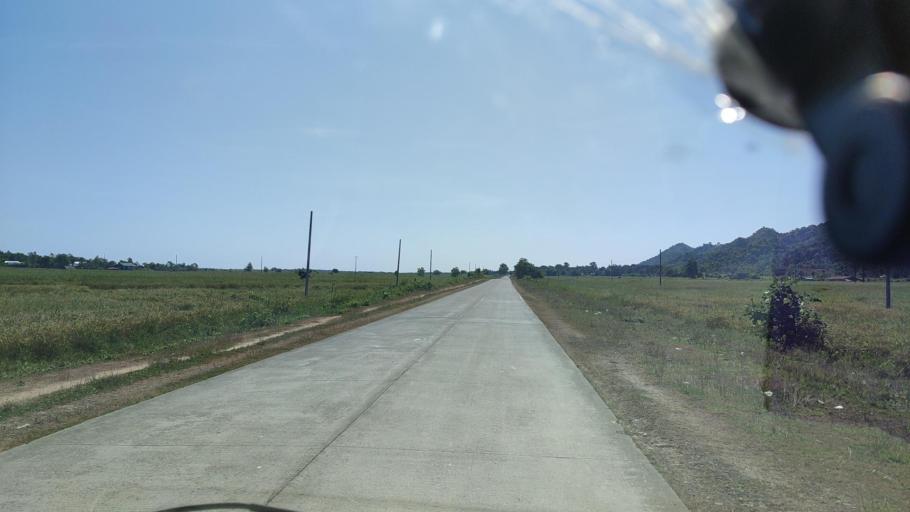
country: MM
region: Rakhine
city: Sittwe
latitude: 20.5547
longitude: 92.9752
